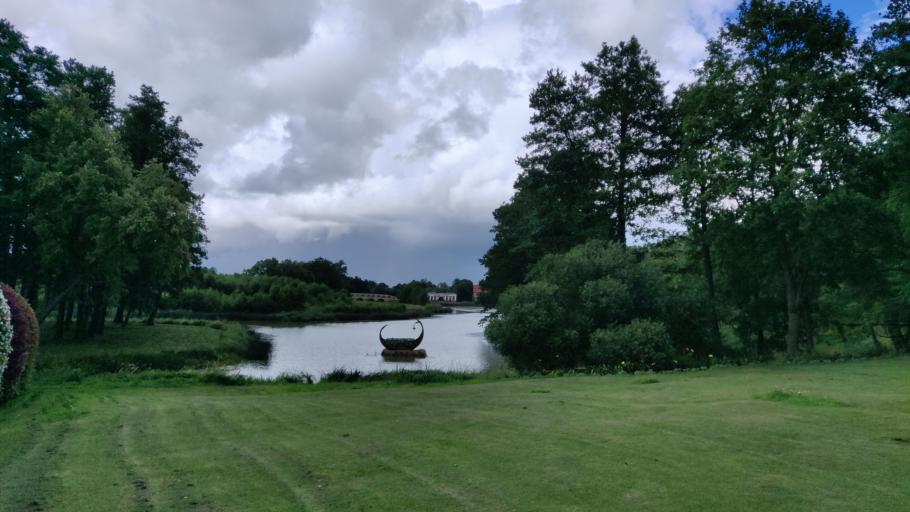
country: LT
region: Siauliu apskritis
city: Pakruojis
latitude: 55.9870
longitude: 23.8795
